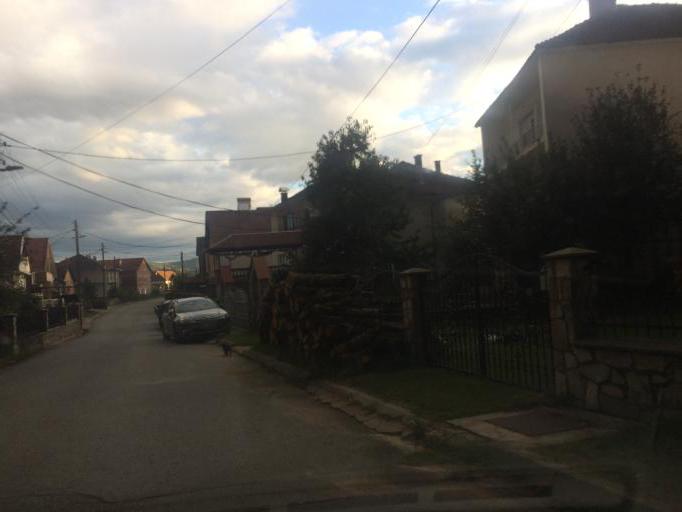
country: MK
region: Makedonska Kamenica
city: Makedonska Kamenica
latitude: 42.0266
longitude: 22.5853
